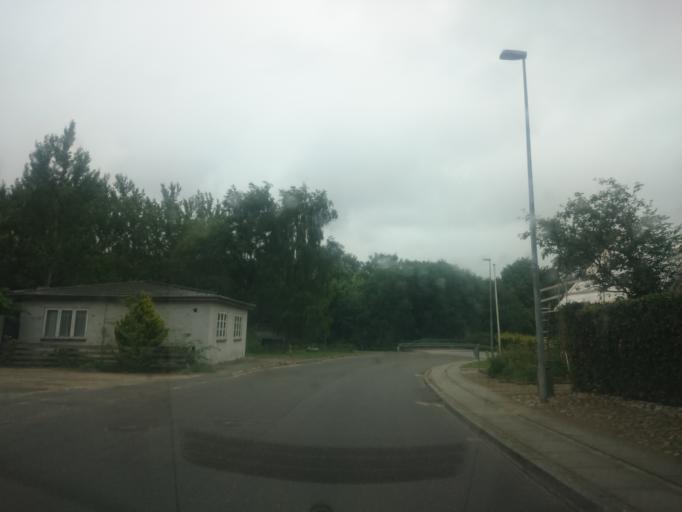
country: DK
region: South Denmark
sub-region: Vejen Kommune
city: Holsted
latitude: 55.5975
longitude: 8.8023
